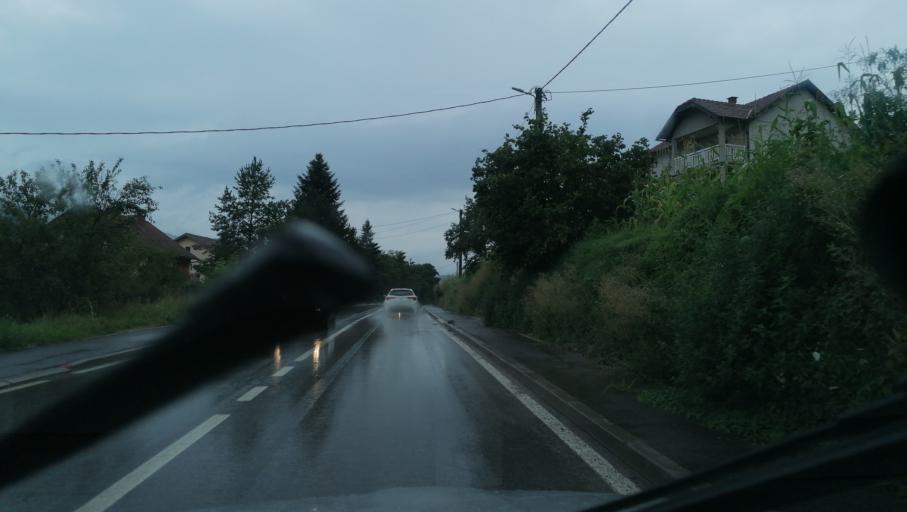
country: BA
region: Federation of Bosnia and Herzegovina
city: Gorazde
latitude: 43.6779
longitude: 18.9870
